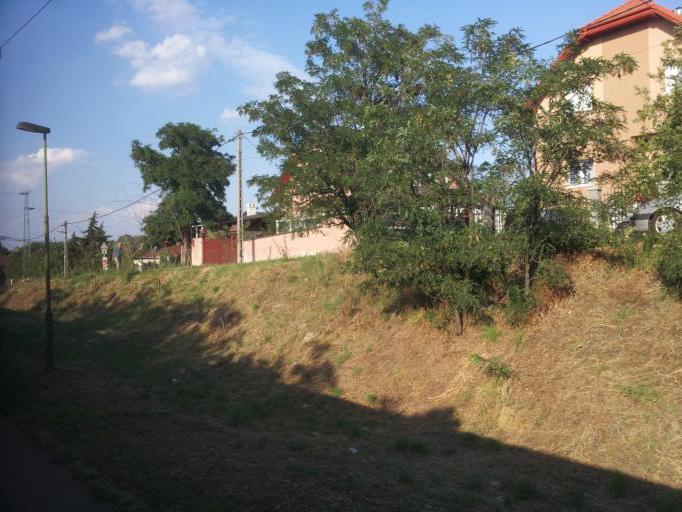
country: HU
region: Pest
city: Dunaharaszti
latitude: 47.3395
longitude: 19.0868
